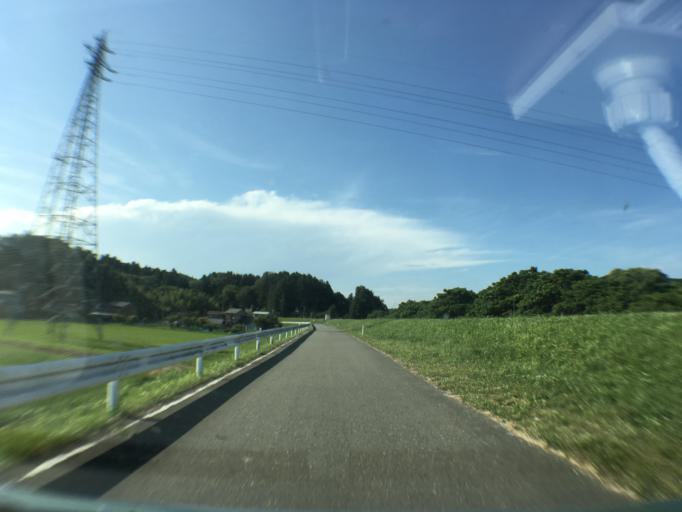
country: JP
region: Miyagi
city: Wakuya
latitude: 38.6174
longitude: 141.2933
